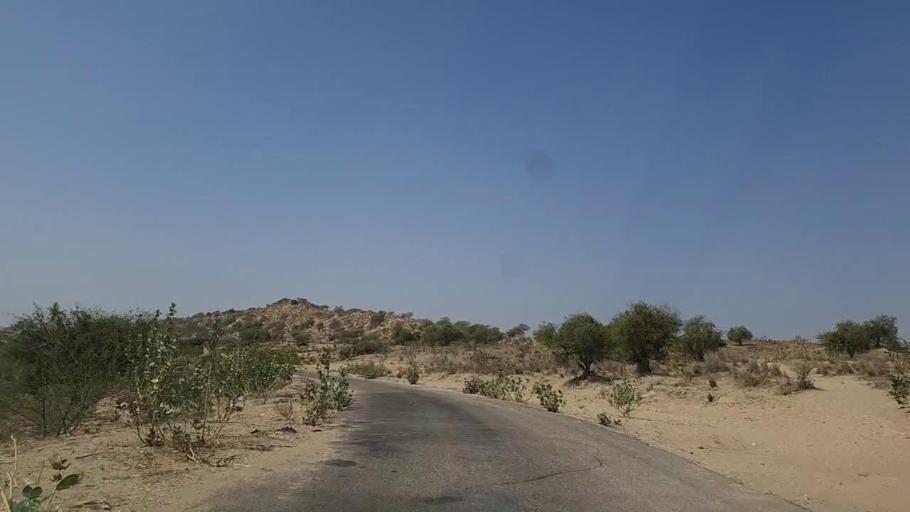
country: PK
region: Sindh
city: Diplo
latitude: 24.5745
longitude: 69.4803
